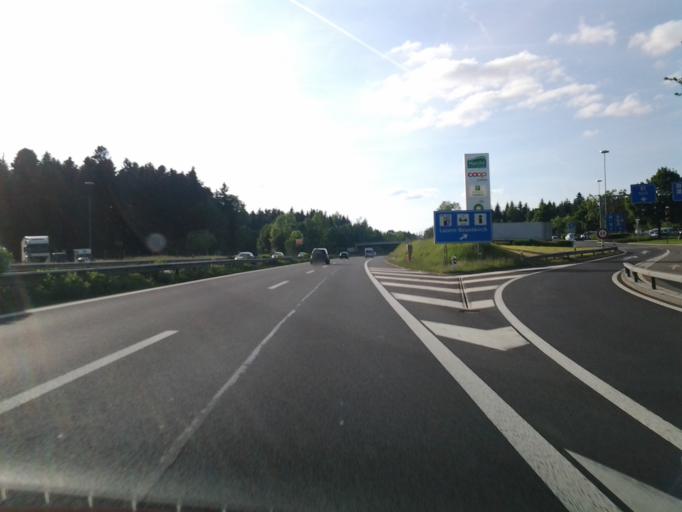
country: CH
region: Lucerne
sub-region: Sursee District
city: Neuenkirch
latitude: 47.1111
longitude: 8.2341
